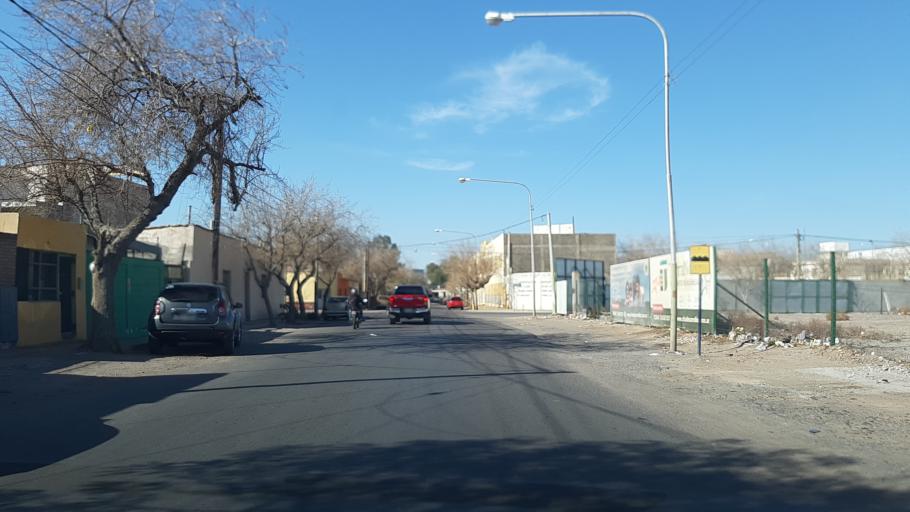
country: AR
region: San Juan
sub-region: Departamento de Santa Lucia
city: Santa Lucia
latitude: -31.5429
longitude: -68.5122
